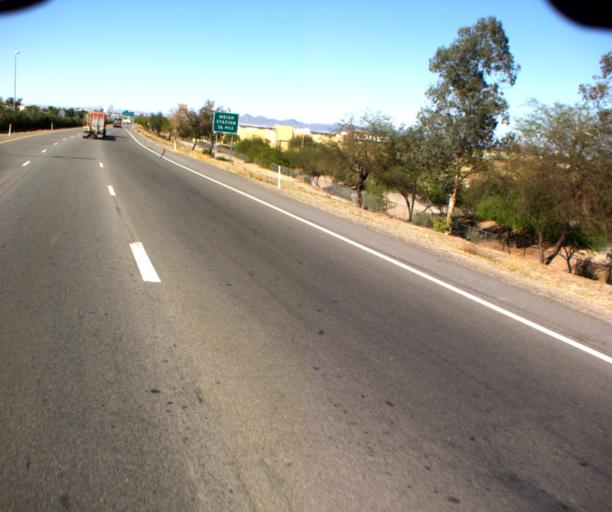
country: US
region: Arizona
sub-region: Yuma County
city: Yuma
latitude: 32.7024
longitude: -114.6096
